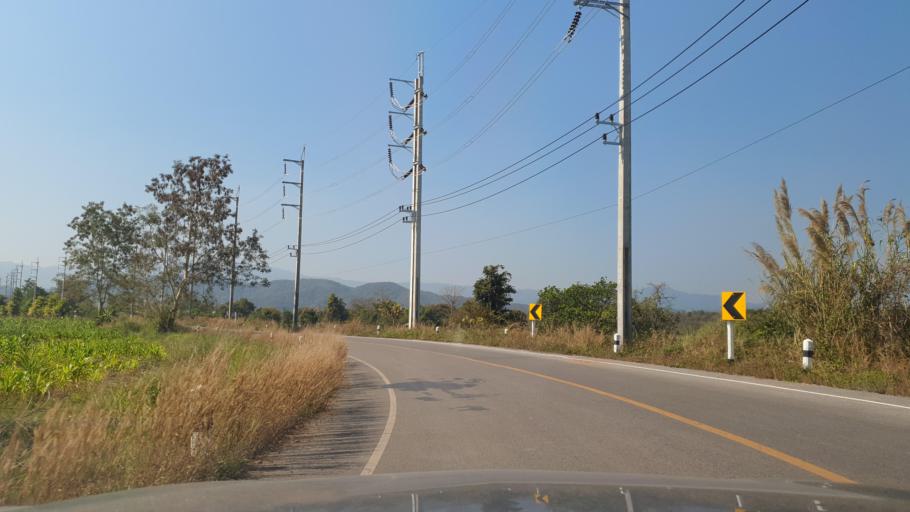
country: TH
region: Chiang Rai
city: Mae Lao
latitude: 19.8018
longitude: 99.6956
